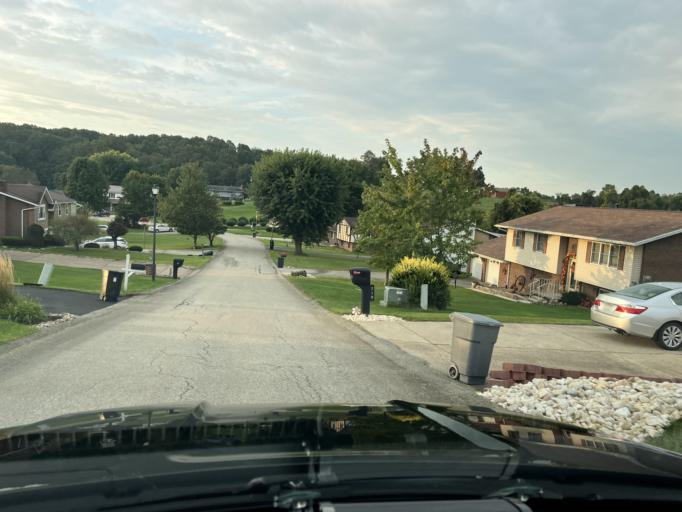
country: US
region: Pennsylvania
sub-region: Fayette County
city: South Uniontown
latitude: 39.8946
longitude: -79.7690
